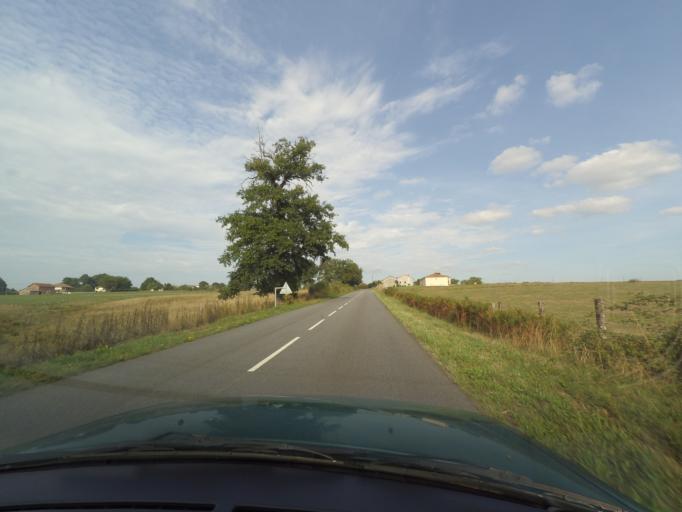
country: FR
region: Limousin
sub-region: Departement de la Haute-Vienne
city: Saint-Laurent-sur-Gorre
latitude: 45.7683
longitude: 0.9790
